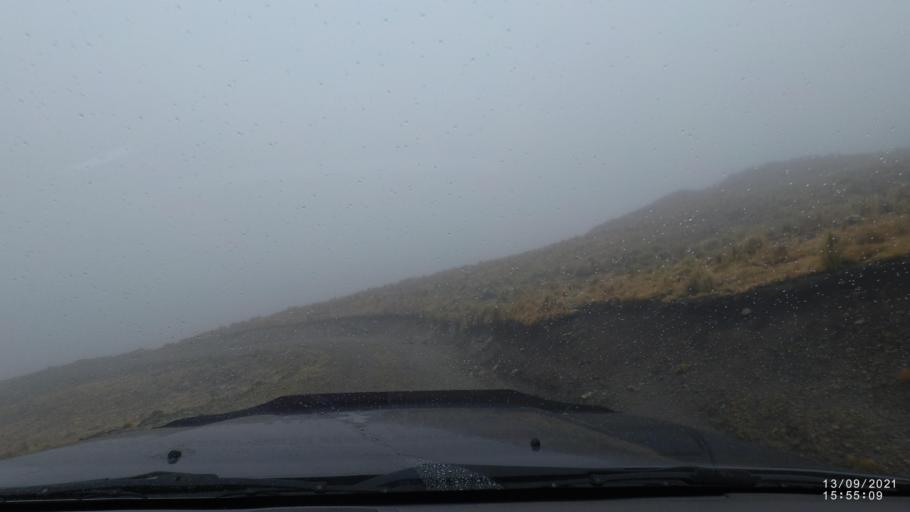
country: BO
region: Cochabamba
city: Colomi
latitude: -17.3070
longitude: -65.7054
